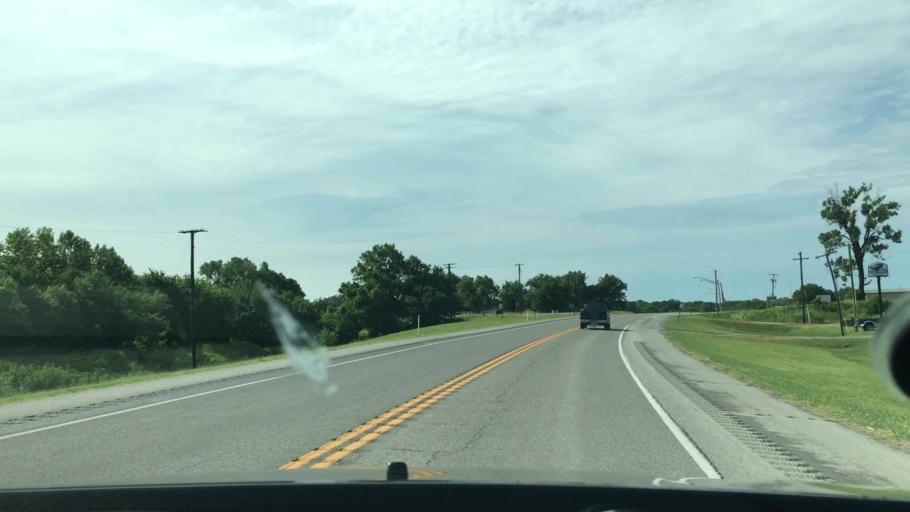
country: US
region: Oklahoma
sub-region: Murray County
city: Sulphur
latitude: 34.5224
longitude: -96.9691
